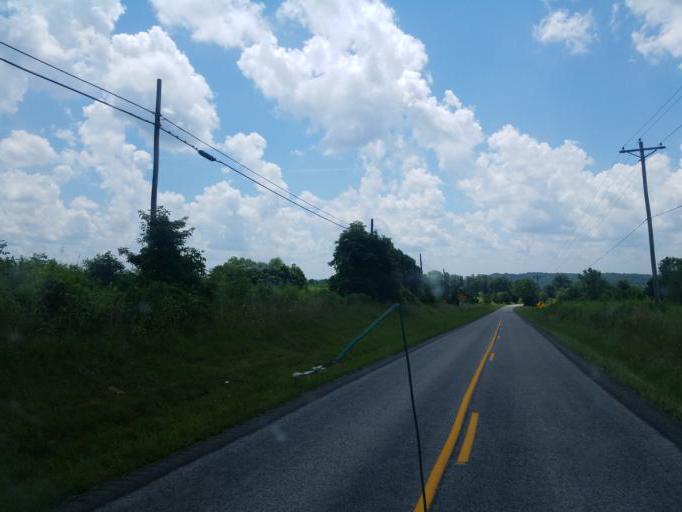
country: US
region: Kentucky
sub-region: Grayson County
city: Leitchfield
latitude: 37.4871
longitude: -86.4761
